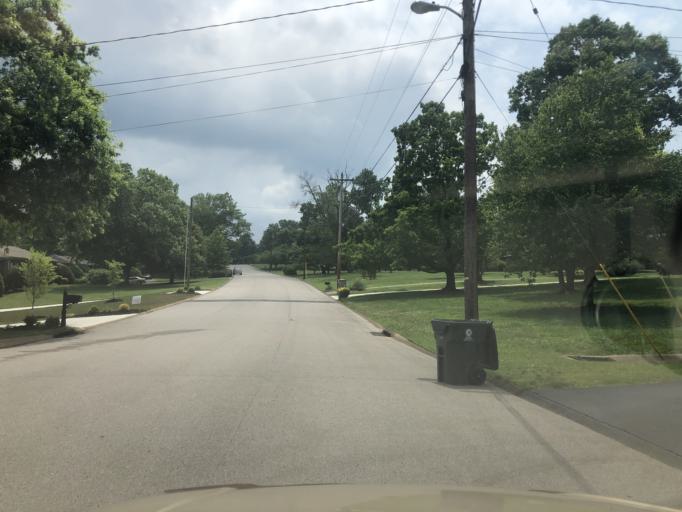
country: US
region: Tennessee
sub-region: Davidson County
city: Lakewood
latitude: 36.2375
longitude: -86.6196
